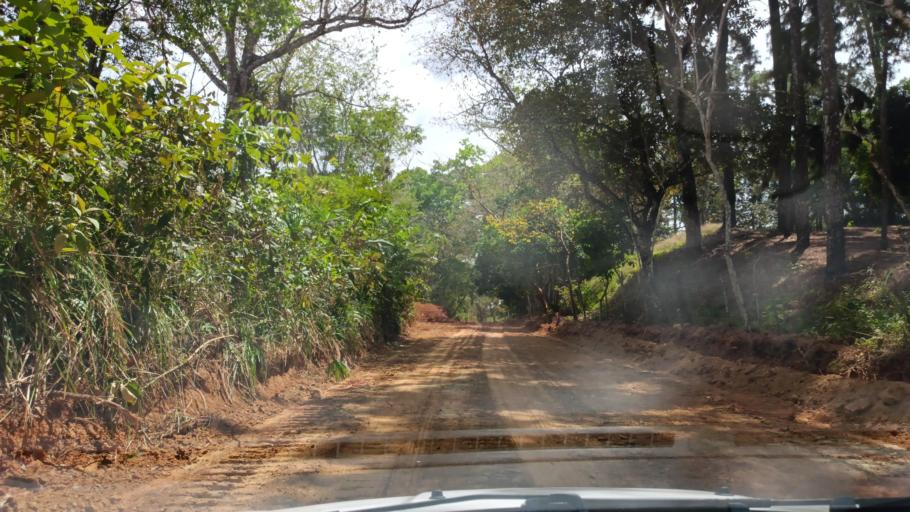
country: PA
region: Panama
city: La Cabima
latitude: 9.1230
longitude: -79.4956
